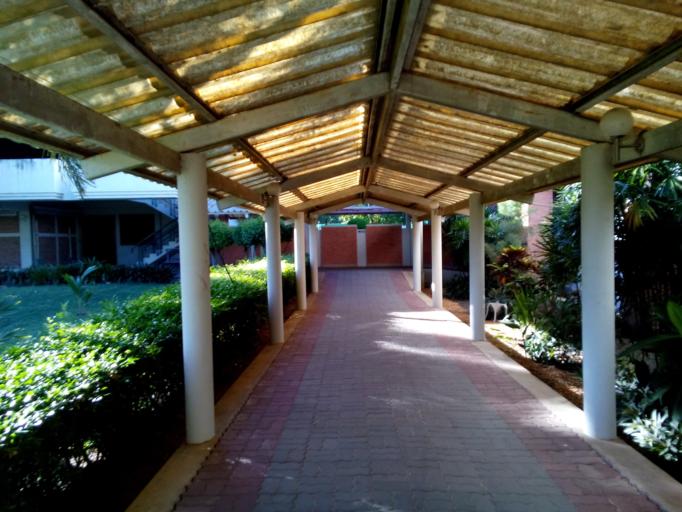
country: TH
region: Chon Buri
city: Phatthaya
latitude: 12.9174
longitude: 100.9946
